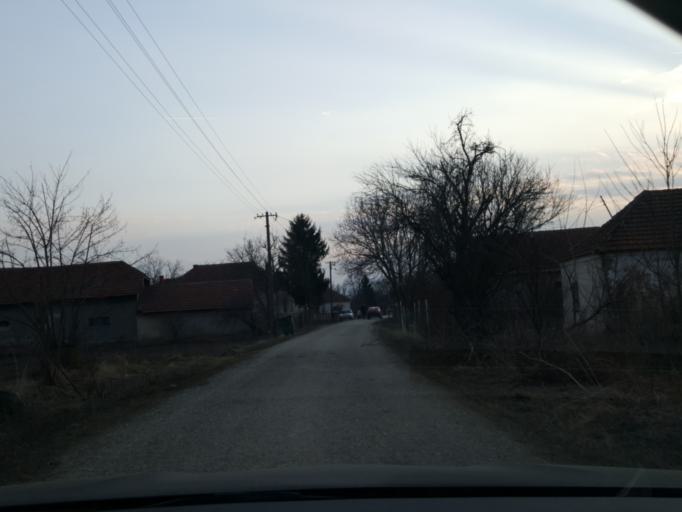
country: RS
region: Central Serbia
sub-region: Nisavski Okrug
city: Aleksinac
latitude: 43.5809
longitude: 21.6470
